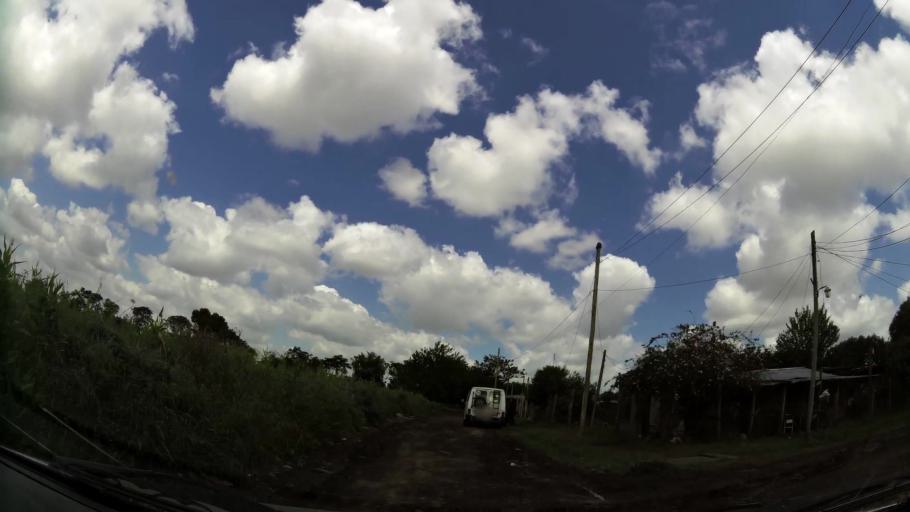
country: AR
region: Buenos Aires
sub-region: Partido de Quilmes
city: Quilmes
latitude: -34.8365
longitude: -58.2236
